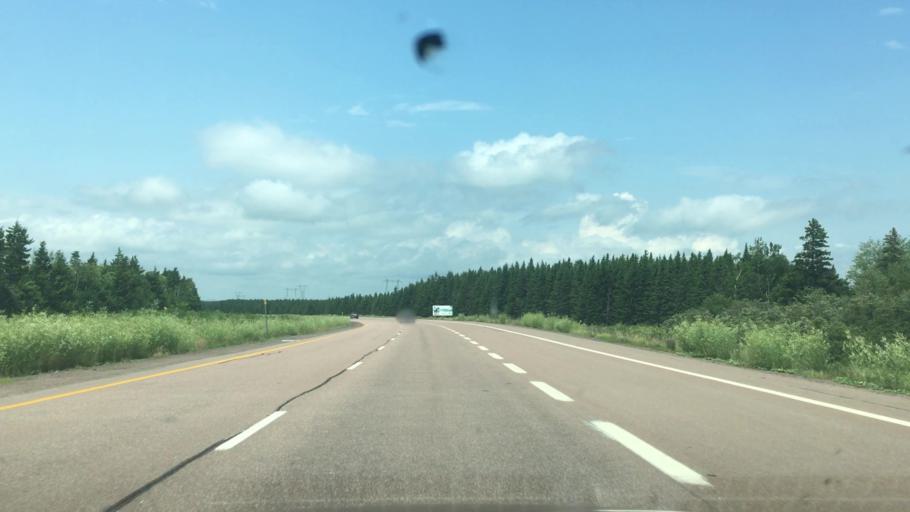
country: CA
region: New Brunswick
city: Sackville
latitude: 45.9648
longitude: -64.4221
